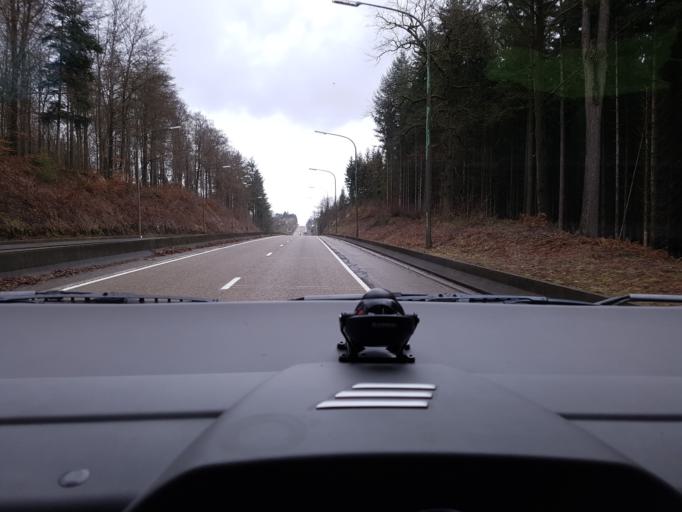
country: BE
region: Wallonia
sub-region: Province du Luxembourg
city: Tenneville
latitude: 50.0952
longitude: 5.4848
